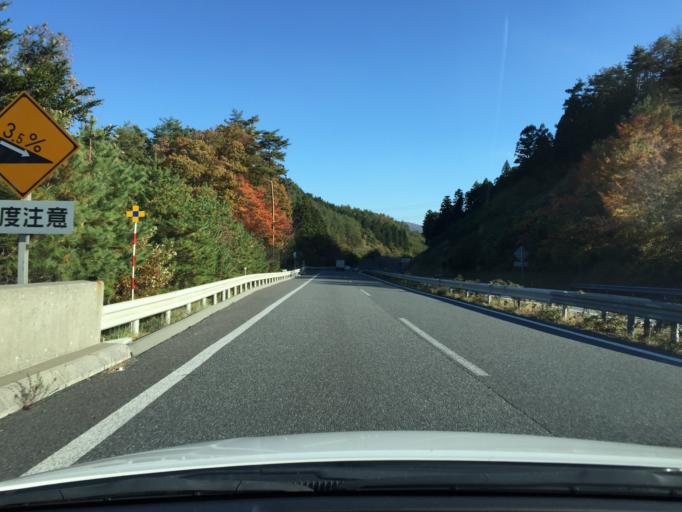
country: JP
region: Fukushima
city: Iwaki
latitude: 37.1523
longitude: 140.7373
